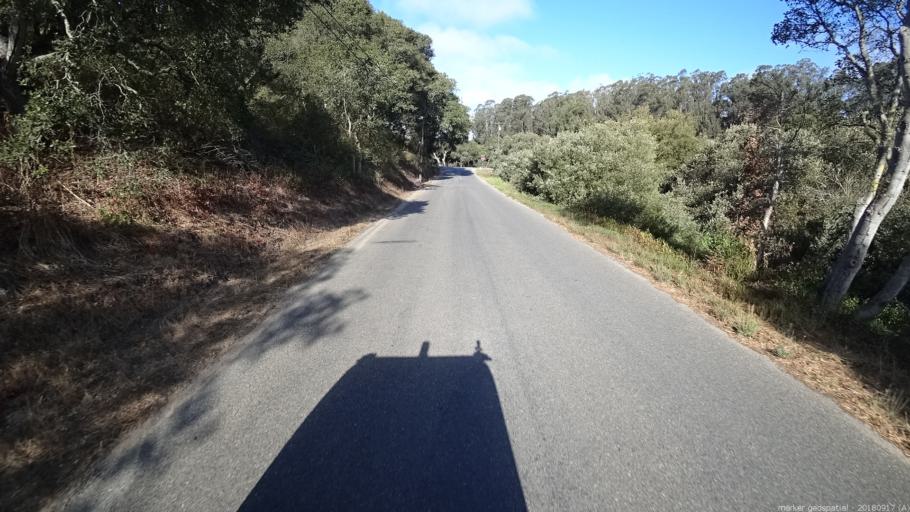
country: US
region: California
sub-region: Monterey County
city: Elkhorn
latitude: 36.8146
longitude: -121.7196
